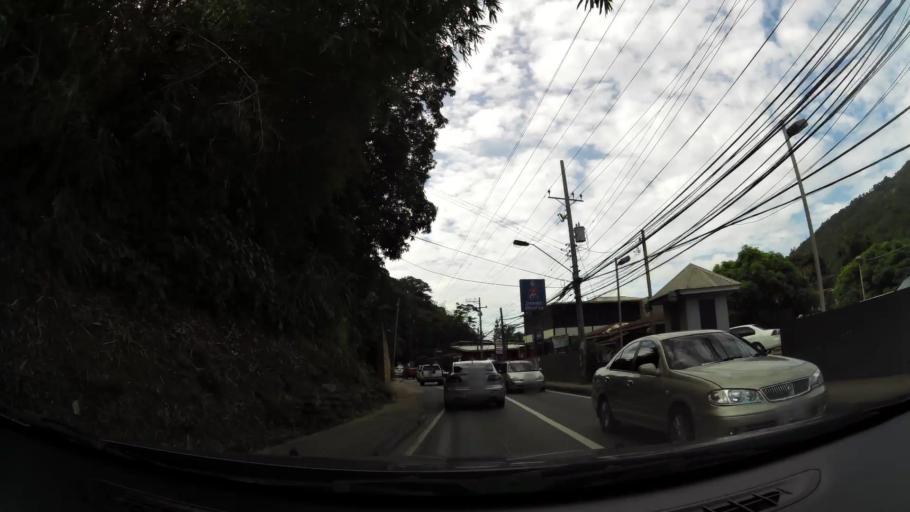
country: TT
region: Diego Martin
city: Petit Valley
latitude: 10.6918
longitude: -61.5183
